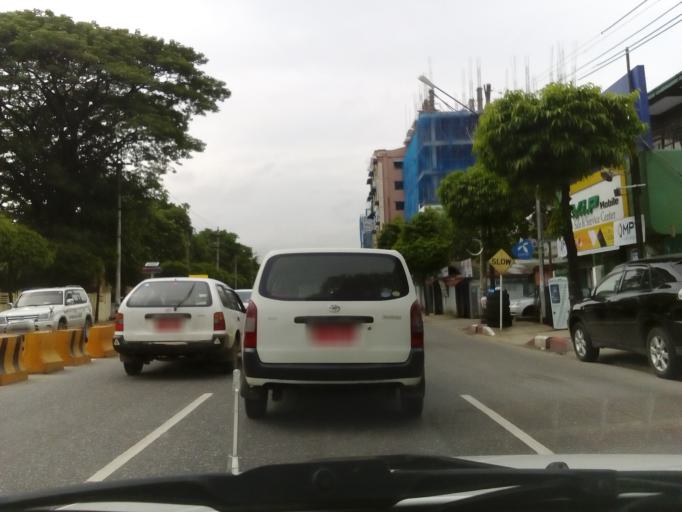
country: MM
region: Yangon
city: Yangon
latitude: 16.8594
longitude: 96.1560
